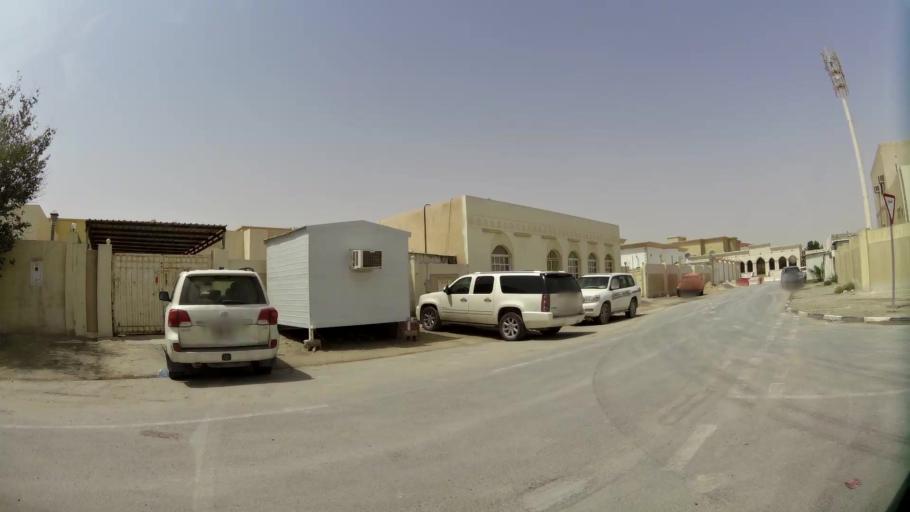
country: QA
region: Baladiyat ar Rayyan
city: Ar Rayyan
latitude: 25.2341
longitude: 51.4170
